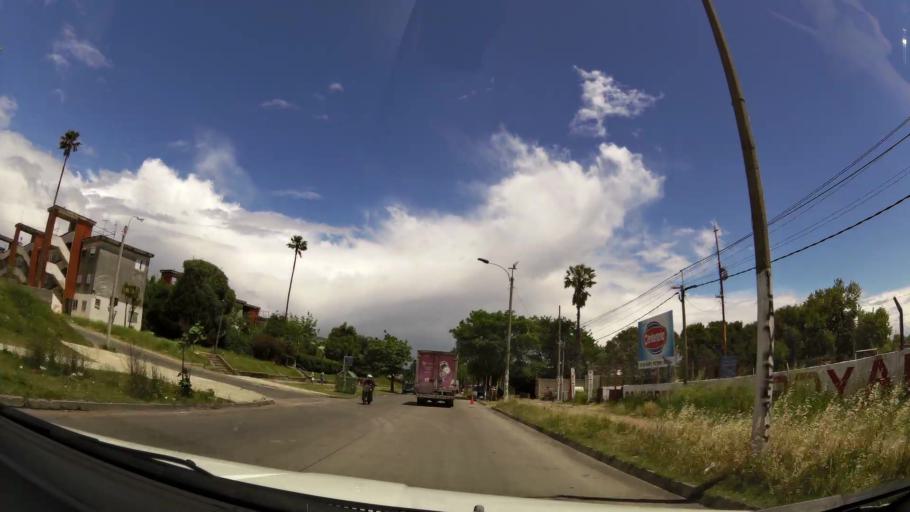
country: UY
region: Montevideo
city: Montevideo
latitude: -34.8397
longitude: -56.1959
